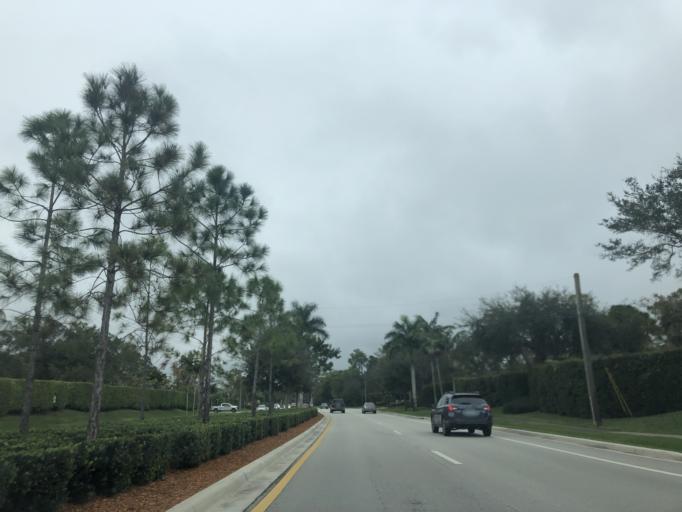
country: US
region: Florida
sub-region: Palm Beach County
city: Wellington
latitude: 26.6687
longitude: -80.2460
